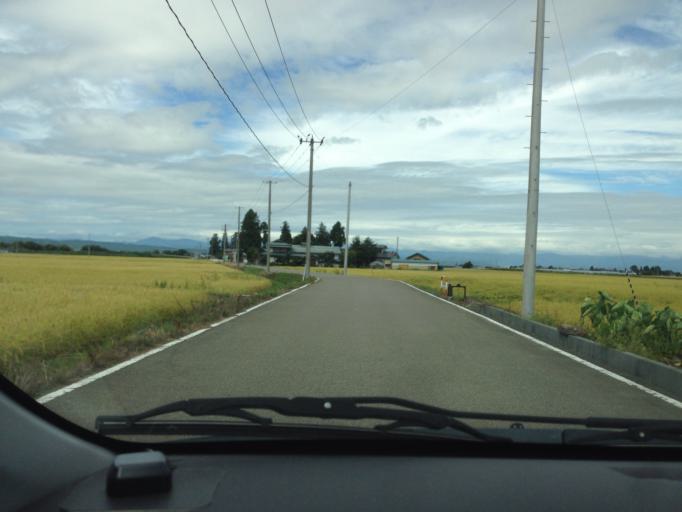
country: JP
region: Fukushima
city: Kitakata
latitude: 37.4812
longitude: 139.8572
